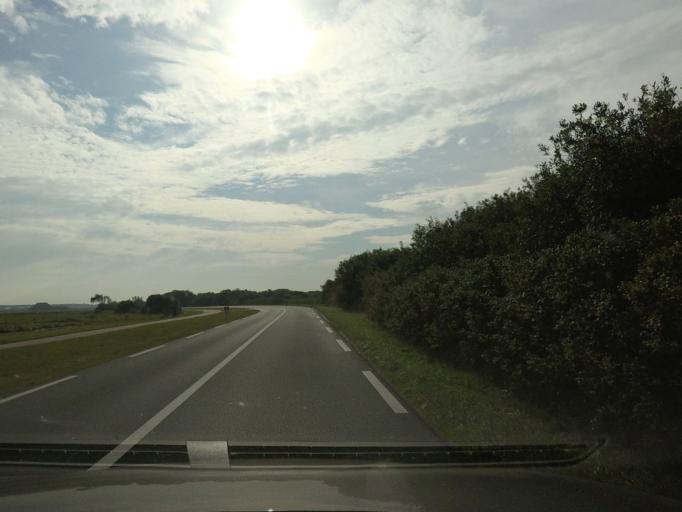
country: NL
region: North Holland
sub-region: Gemeente Schagen
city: Schagen
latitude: 52.8109
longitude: 4.7022
